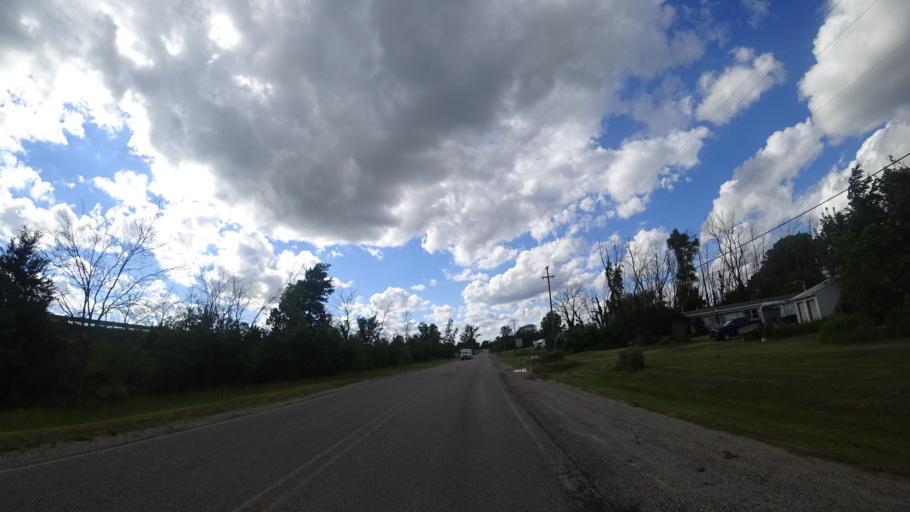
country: US
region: Michigan
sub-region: Ionia County
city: Portland
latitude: 42.8723
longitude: -84.9627
